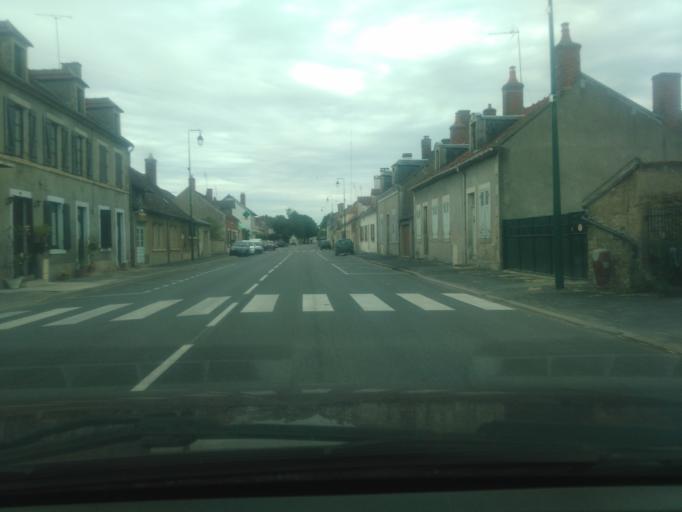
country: FR
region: Centre
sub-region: Departement du Cher
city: Charenton-du-Cher
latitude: 46.7314
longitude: 2.6348
